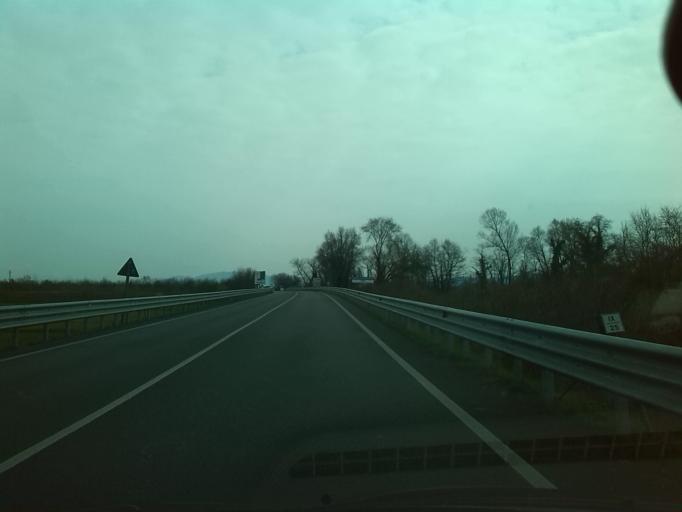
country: IT
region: Friuli Venezia Giulia
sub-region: Provincia di Gorizia
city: Moraro
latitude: 45.9430
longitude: 13.4946
